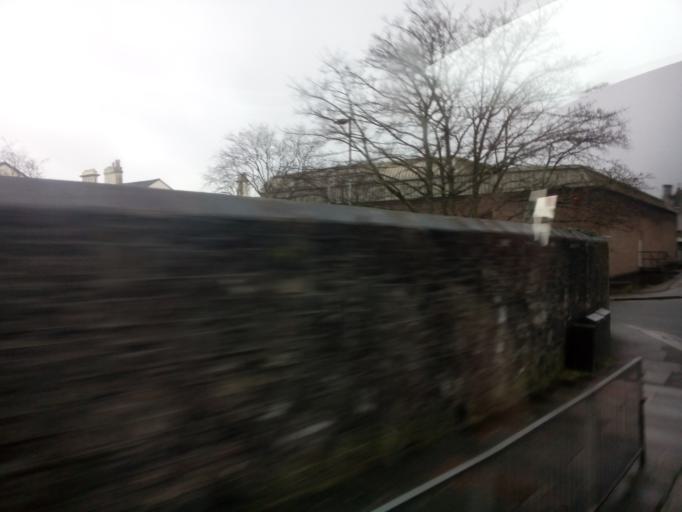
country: GB
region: England
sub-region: Plymouth
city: Plymouth
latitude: 50.3844
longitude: -4.1353
